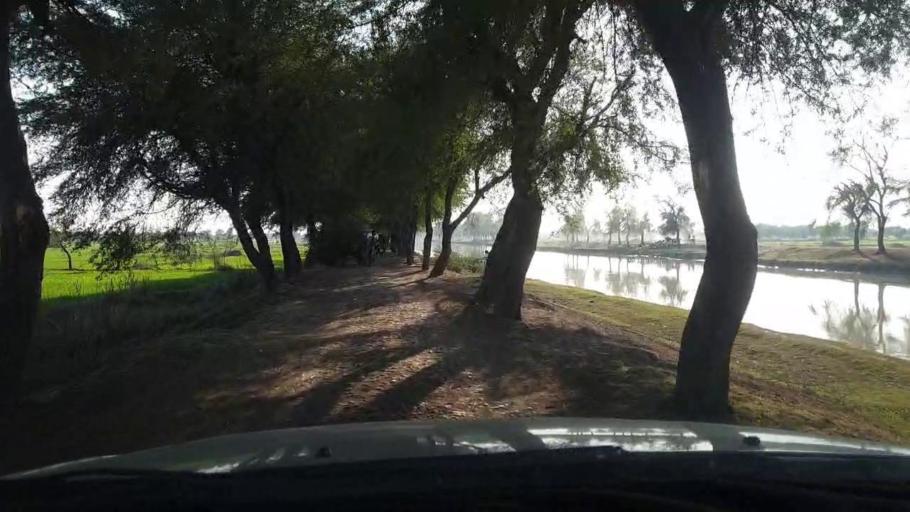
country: PK
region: Sindh
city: Mirpur Mathelo
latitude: 27.9700
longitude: 69.5238
